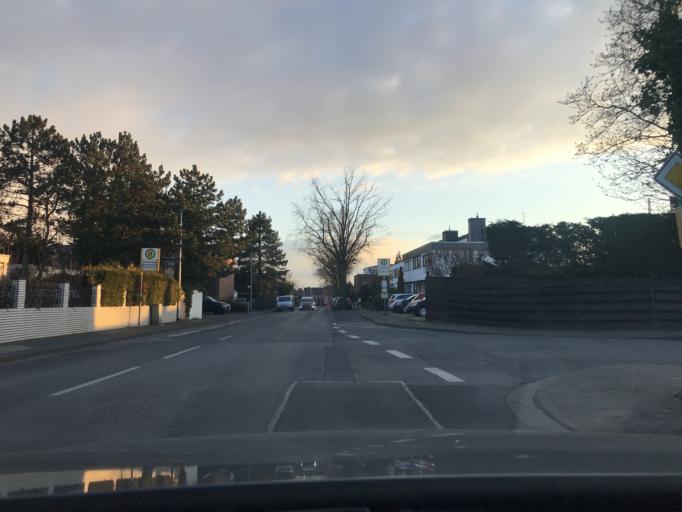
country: DE
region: North Rhine-Westphalia
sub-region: Regierungsbezirk Dusseldorf
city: Kaarst
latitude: 51.2336
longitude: 6.6277
